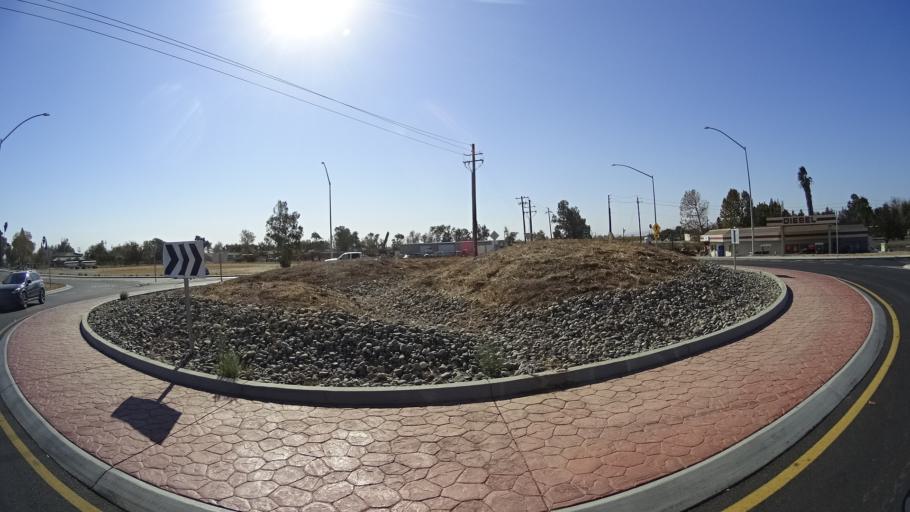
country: US
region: California
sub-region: Yolo County
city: Cottonwood
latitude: 38.6820
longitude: -121.9672
